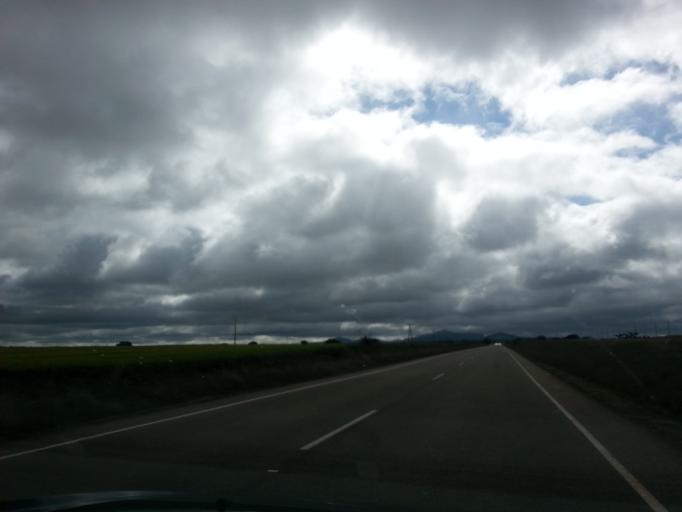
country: ES
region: Castille and Leon
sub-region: Provincia de Salamanca
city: Abusejo
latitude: 40.7049
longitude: -6.1393
